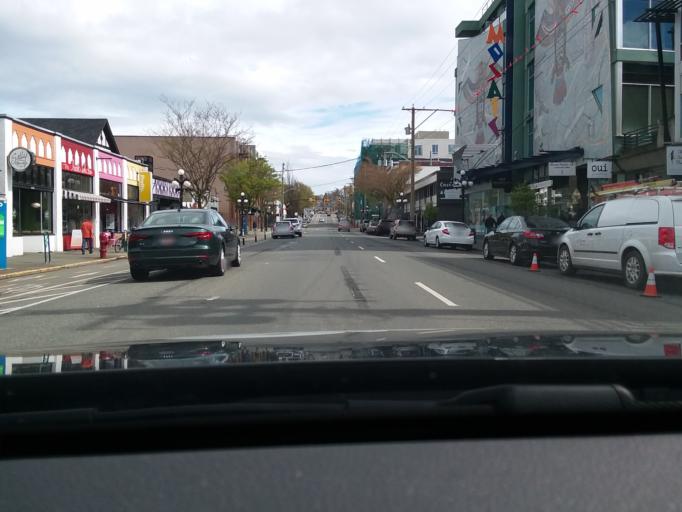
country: CA
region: British Columbia
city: Victoria
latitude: 48.4236
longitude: -123.3558
